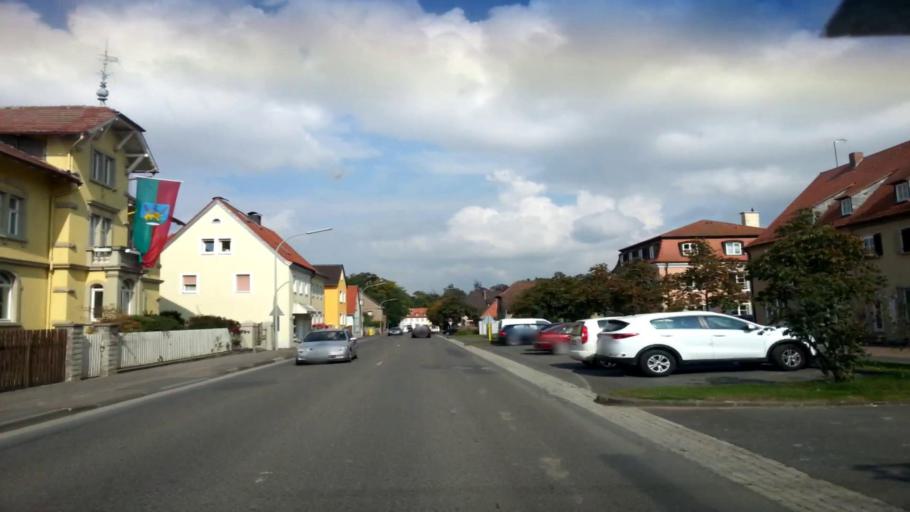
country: DE
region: Bavaria
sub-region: Regierungsbezirk Unterfranken
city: Wiesentheid
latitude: 49.7907
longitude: 10.3410
